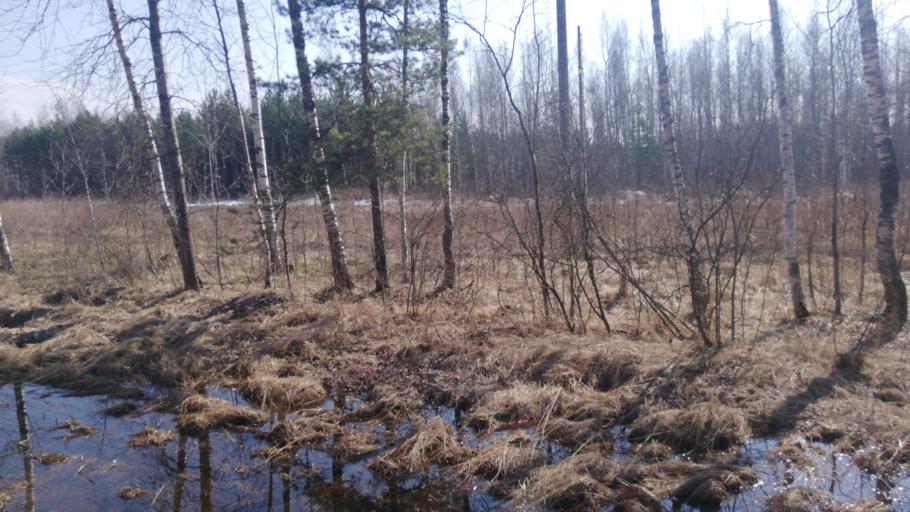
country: RU
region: Jaroslavl
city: Rostov
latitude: 57.2356
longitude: 39.4800
